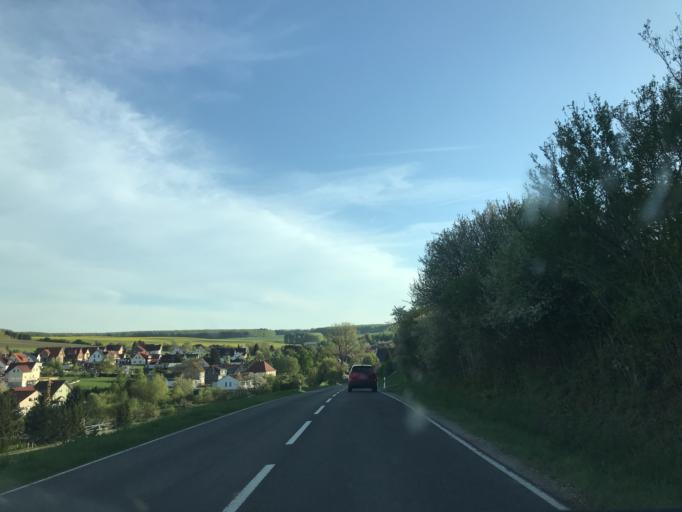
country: DE
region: Thuringia
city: Heuthen
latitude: 51.3371
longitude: 10.2281
